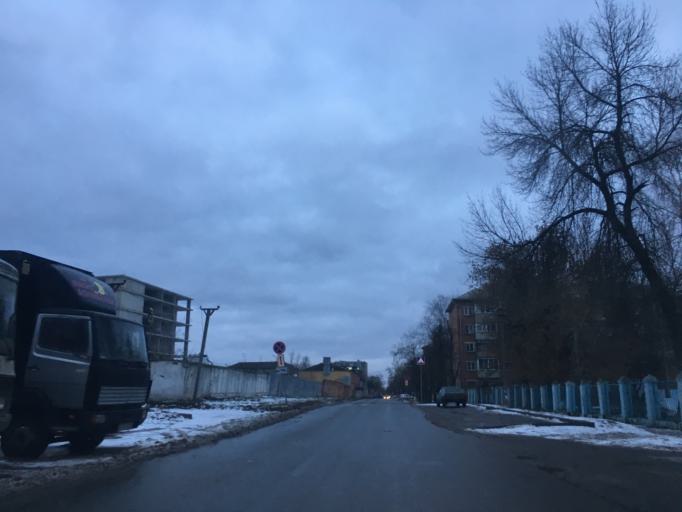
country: RU
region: Tula
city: Tula
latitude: 54.1998
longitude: 37.5873
